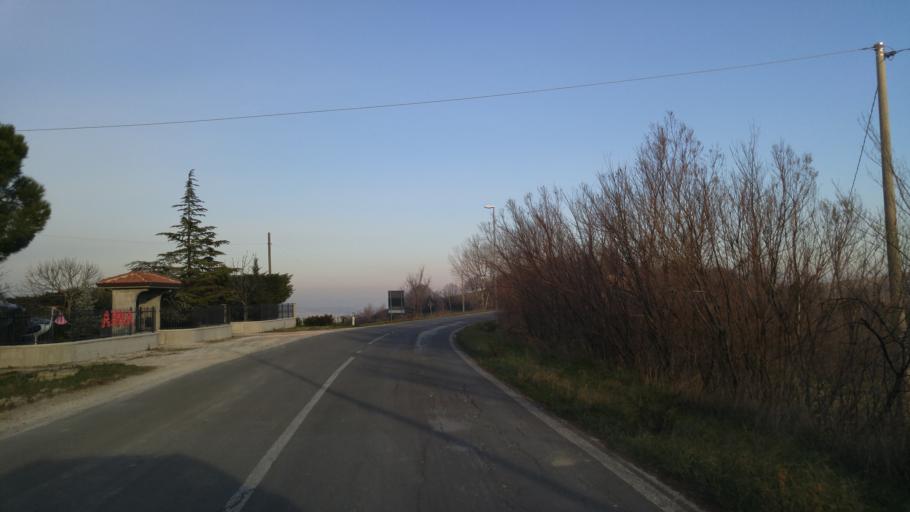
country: IT
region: The Marches
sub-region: Provincia di Pesaro e Urbino
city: San Giorgio di Pesaro
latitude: 43.7102
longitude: 12.9999
